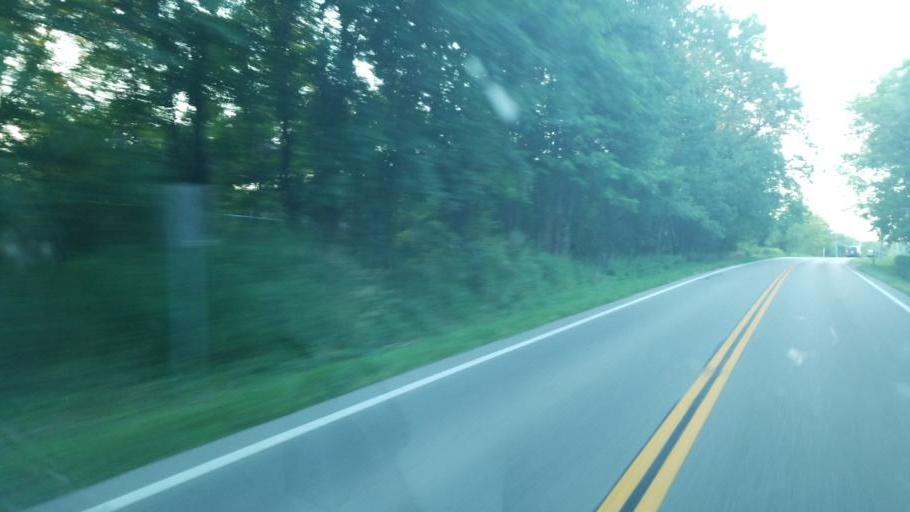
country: US
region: Ohio
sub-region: Trumbull County
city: Newton Falls
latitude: 41.2132
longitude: -80.9796
